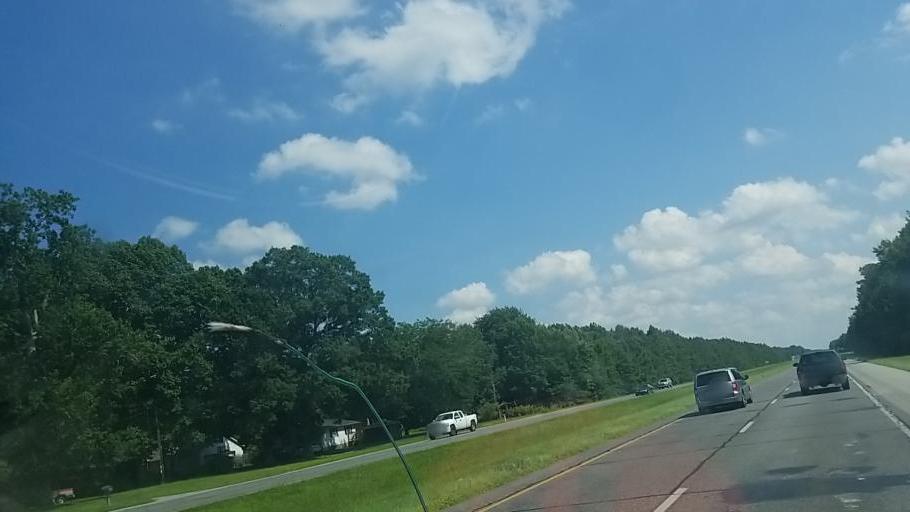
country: US
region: Delaware
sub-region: Sussex County
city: Georgetown
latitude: 38.7470
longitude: -75.4305
